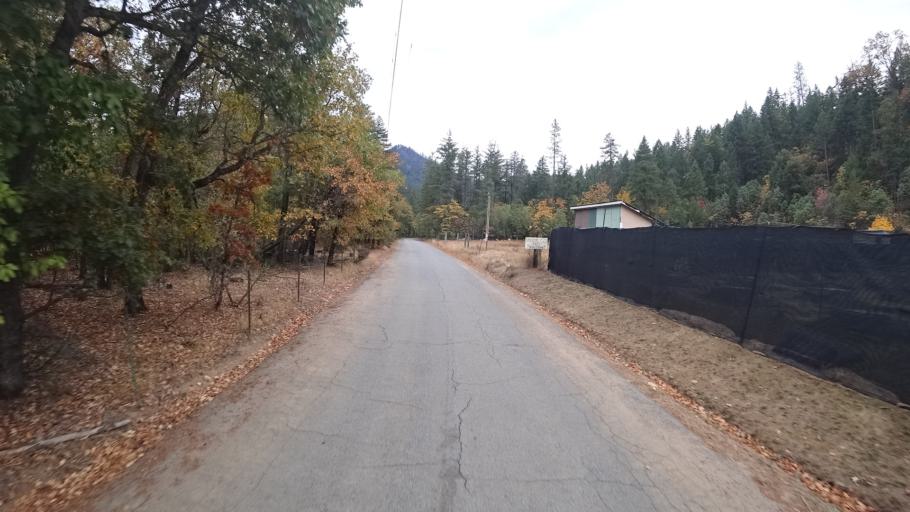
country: US
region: California
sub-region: Siskiyou County
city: Happy Camp
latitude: 41.8307
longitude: -123.1716
